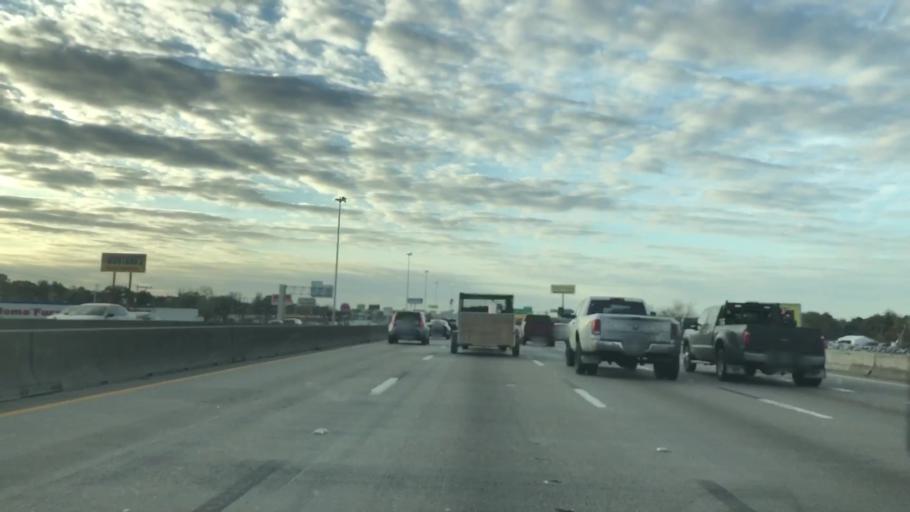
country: US
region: Texas
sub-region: Harris County
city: Aldine
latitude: 29.8980
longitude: -95.4124
